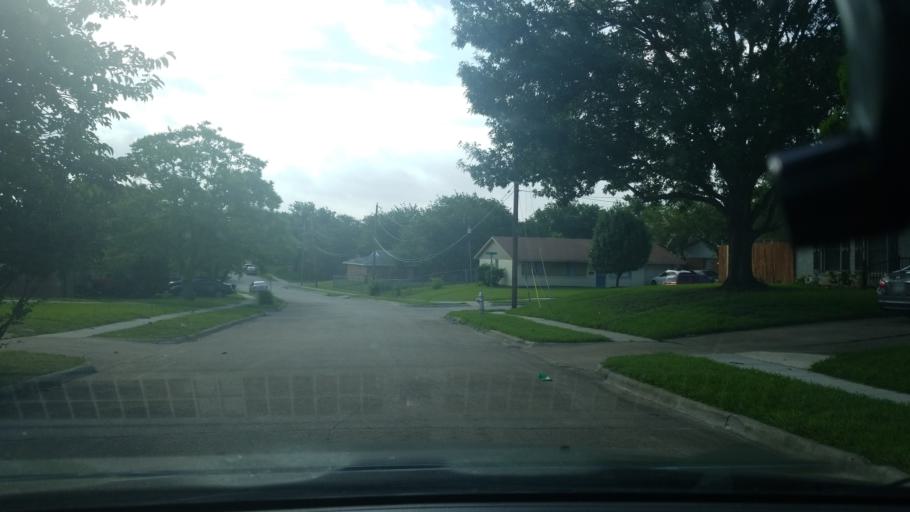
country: US
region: Texas
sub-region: Dallas County
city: Mesquite
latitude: 32.7726
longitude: -96.6414
